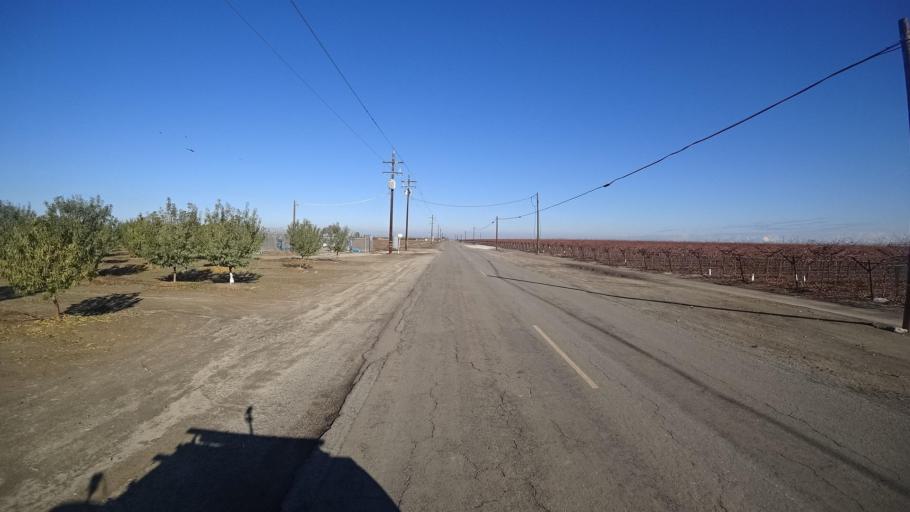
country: US
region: California
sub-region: Kern County
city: McFarland
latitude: 35.7137
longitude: -119.2764
